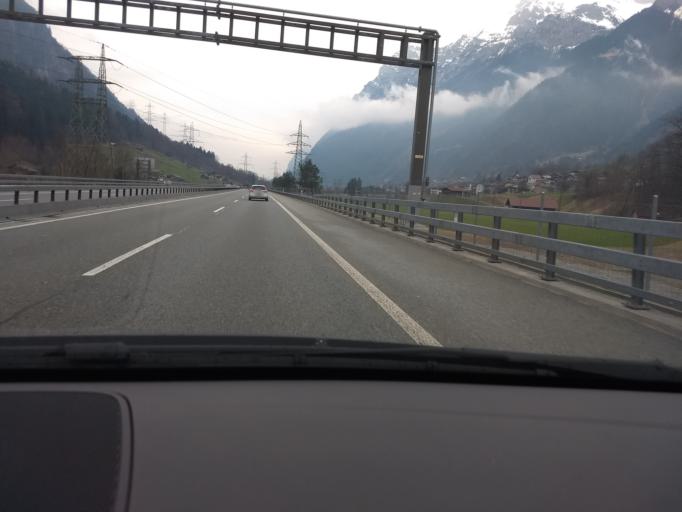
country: CH
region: Uri
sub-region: Uri
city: Silenen
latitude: 46.7863
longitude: 8.6676
